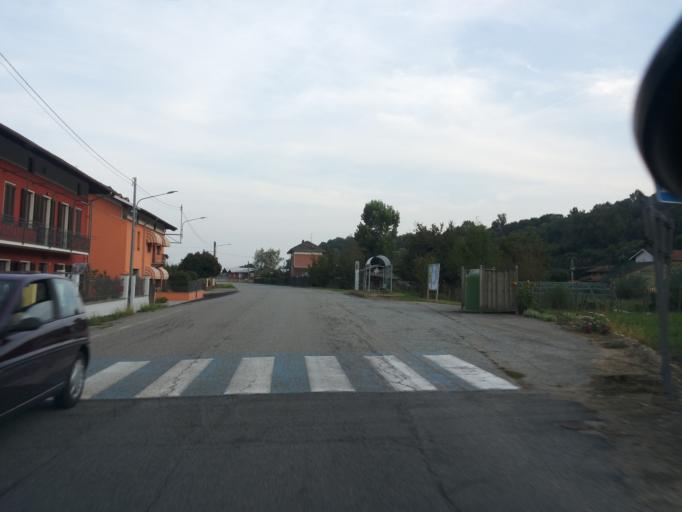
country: IT
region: Piedmont
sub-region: Provincia di Biella
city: Mottalciata
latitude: 45.5164
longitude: 8.2014
